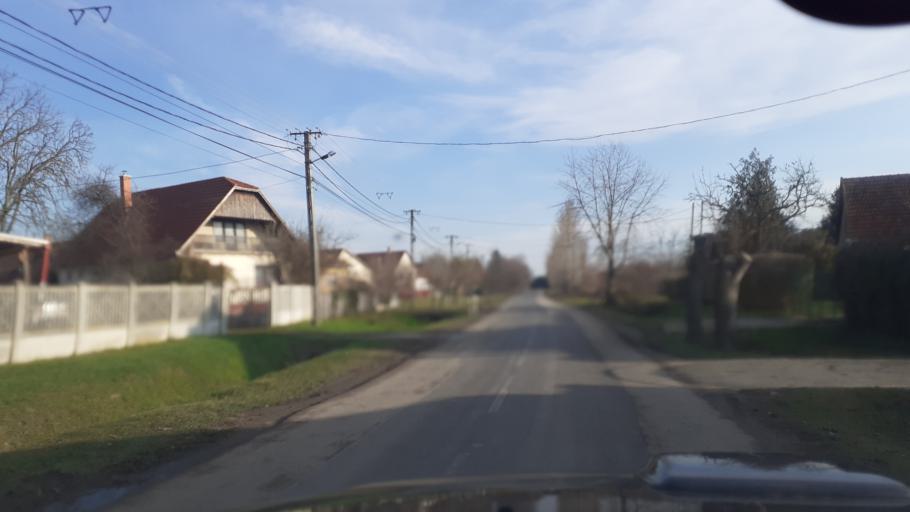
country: HU
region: Pest
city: Domsod
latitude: 47.0910
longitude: 19.0255
